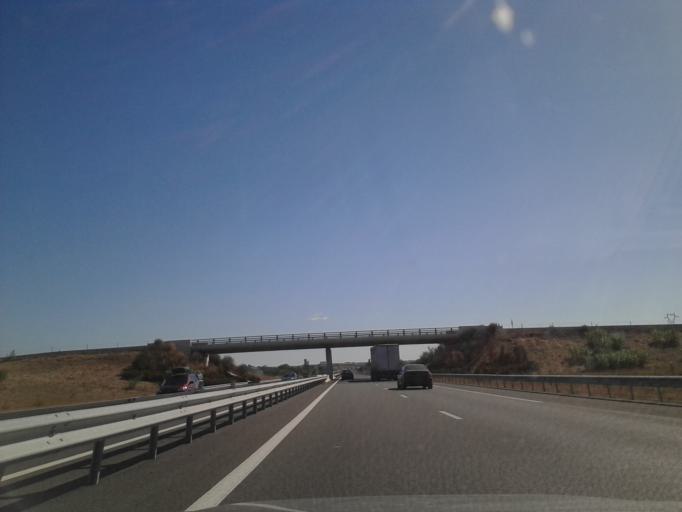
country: FR
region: Languedoc-Roussillon
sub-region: Departement de l'Herault
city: Montblanc
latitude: 43.3978
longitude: 3.3331
